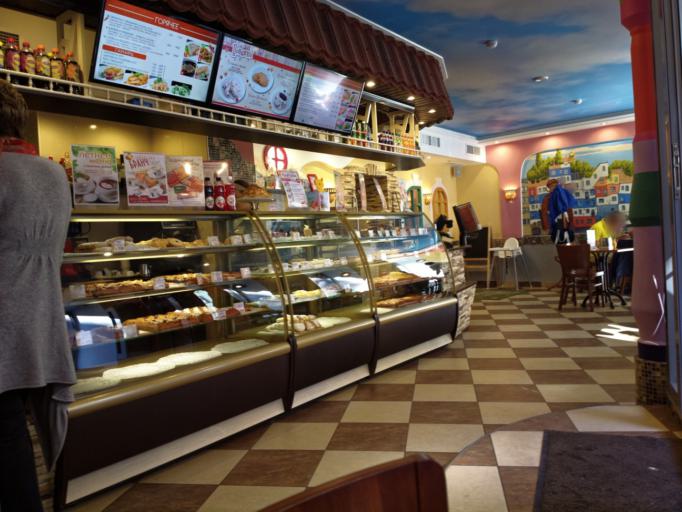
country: RU
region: St.-Petersburg
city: Centralniy
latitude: 59.9257
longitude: 30.3437
